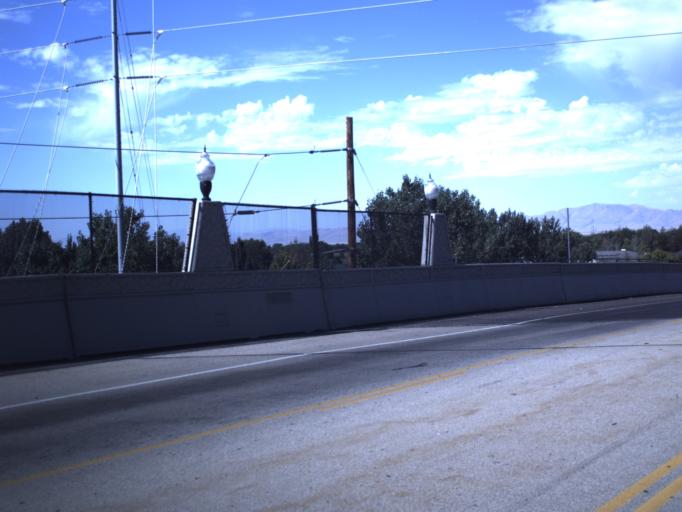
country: US
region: Utah
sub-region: Davis County
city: Kaysville
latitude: 41.0382
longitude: -111.9527
